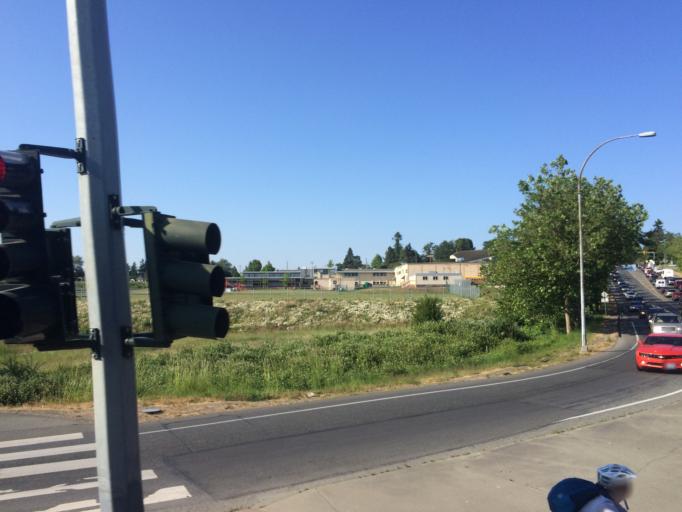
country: CA
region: British Columbia
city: Victoria
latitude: 48.4598
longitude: -123.4047
